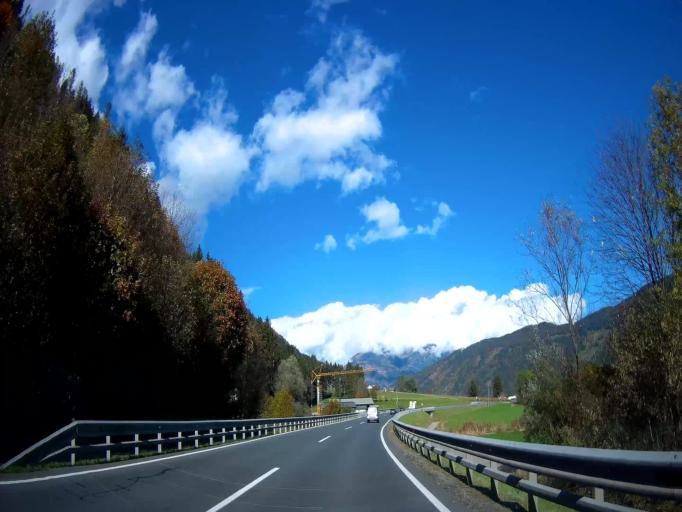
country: AT
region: Carinthia
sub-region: Politischer Bezirk Spittal an der Drau
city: Sachsenburg
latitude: 46.7784
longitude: 13.3445
